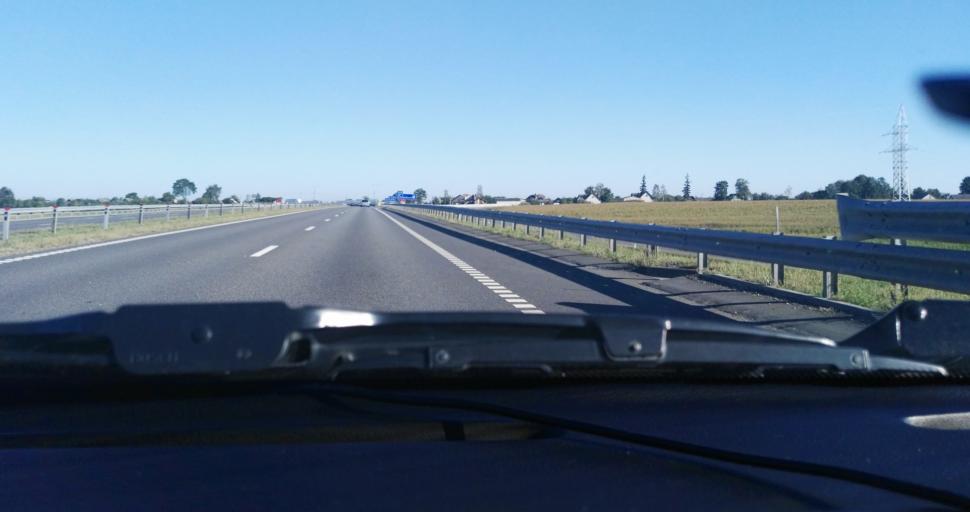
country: BY
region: Gomel
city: Buda-Kashalyova
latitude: 52.5149
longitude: 30.6291
